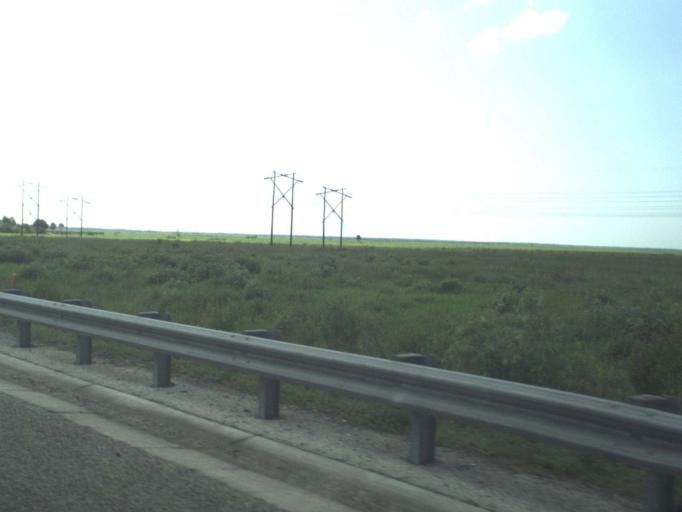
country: US
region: Florida
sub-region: Brevard County
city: Cocoa West
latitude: 28.3691
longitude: -80.8647
